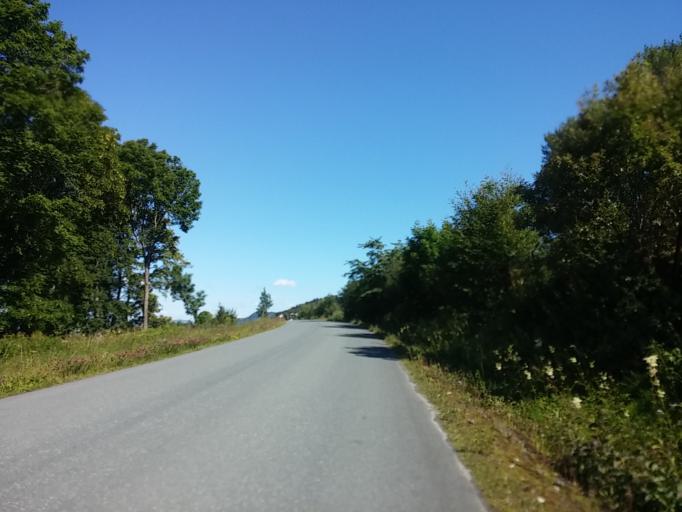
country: NO
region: Sor-Trondelag
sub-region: Malvik
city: Malvik
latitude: 63.4310
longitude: 10.7195
